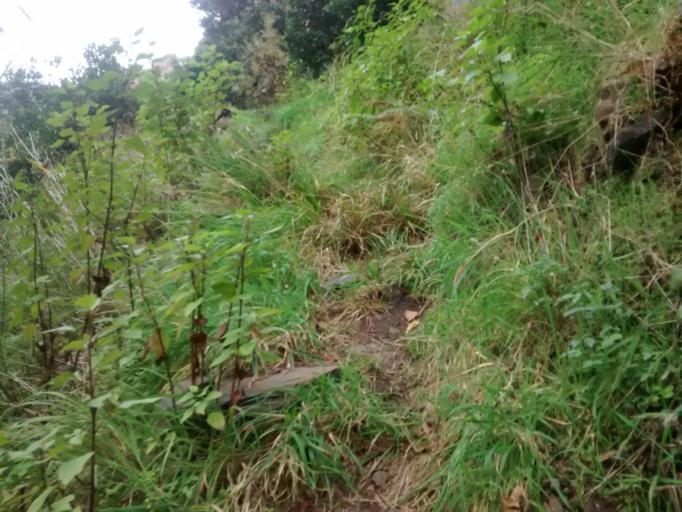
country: PT
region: Madeira
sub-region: Camara de Lobos
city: Curral das Freiras
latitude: 32.7264
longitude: -17.0175
